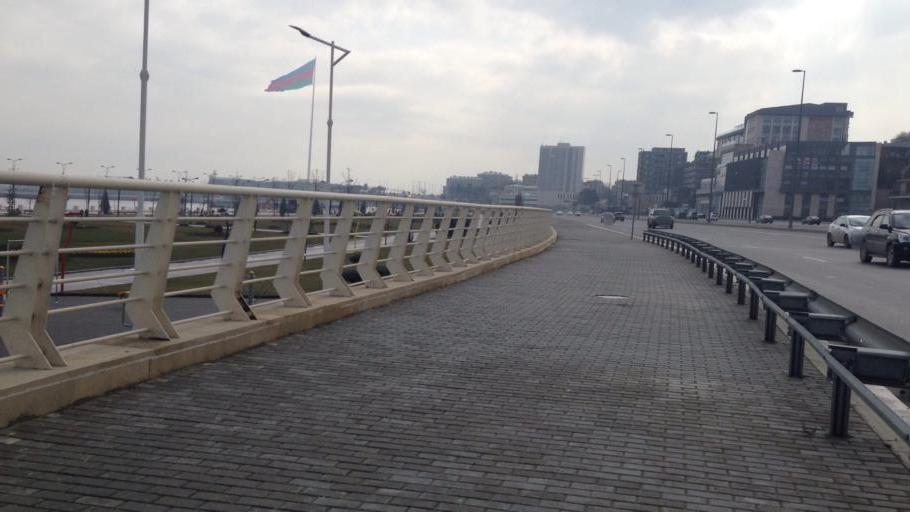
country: AZ
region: Baki
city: Badamdar
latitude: 40.3521
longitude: 49.8347
